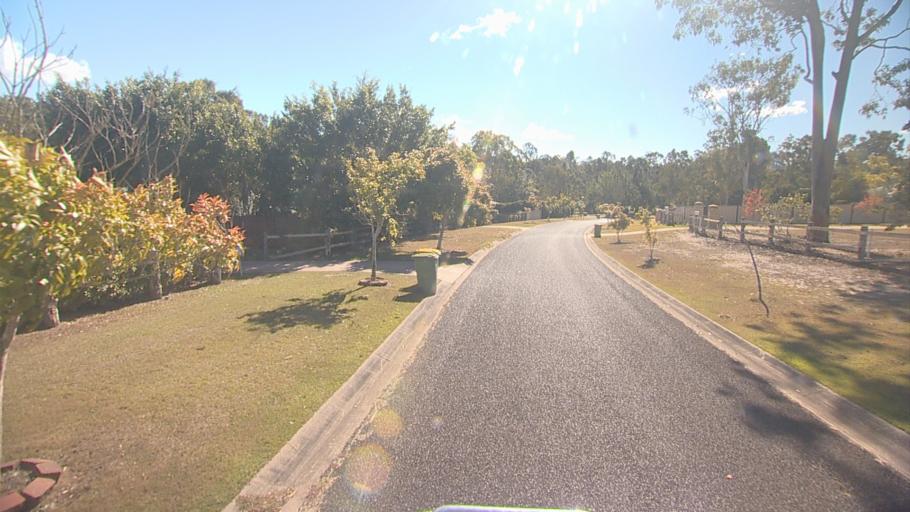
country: AU
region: Queensland
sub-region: Ipswich
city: Springfield Lakes
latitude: -27.7342
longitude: 152.9206
